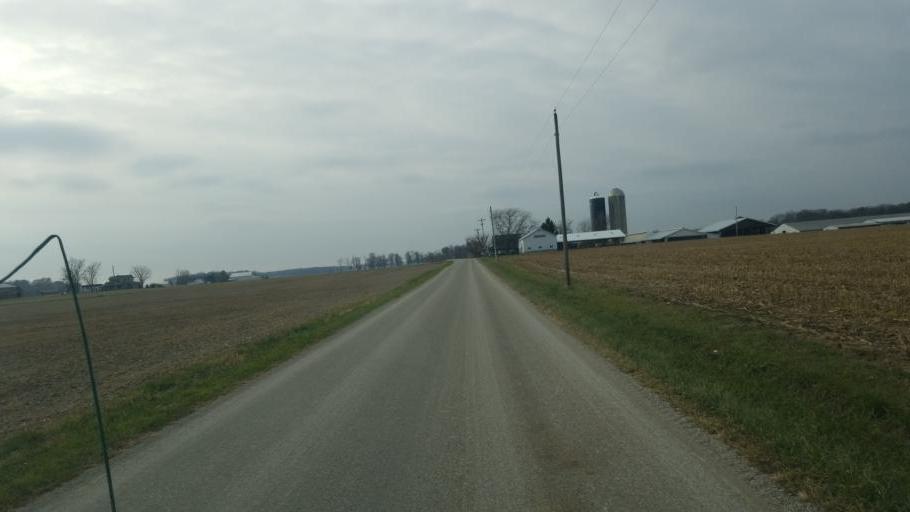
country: US
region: Indiana
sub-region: Adams County
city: Geneva
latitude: 40.6059
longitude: -84.9906
